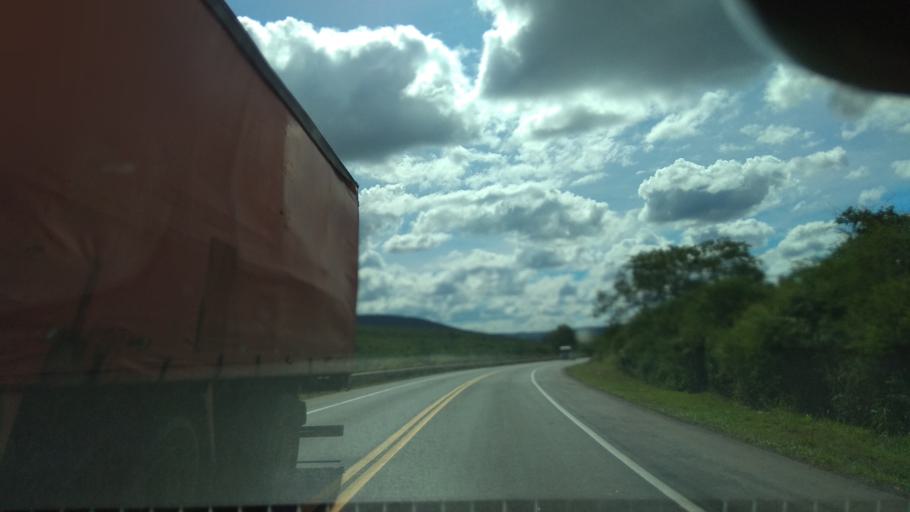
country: BR
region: Bahia
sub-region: Santa Ines
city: Santa Ines
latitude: -13.3081
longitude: -40.0257
